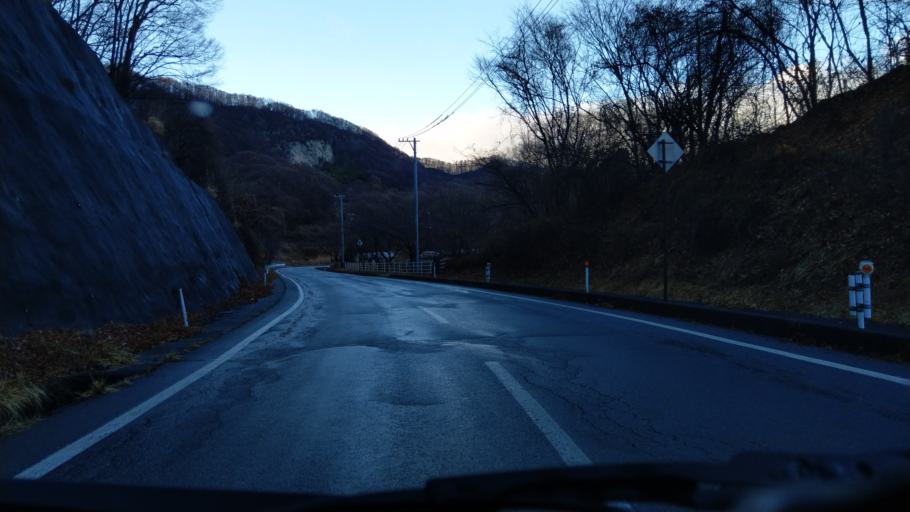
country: JP
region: Nagano
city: Komoro
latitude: 36.3023
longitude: 138.4159
